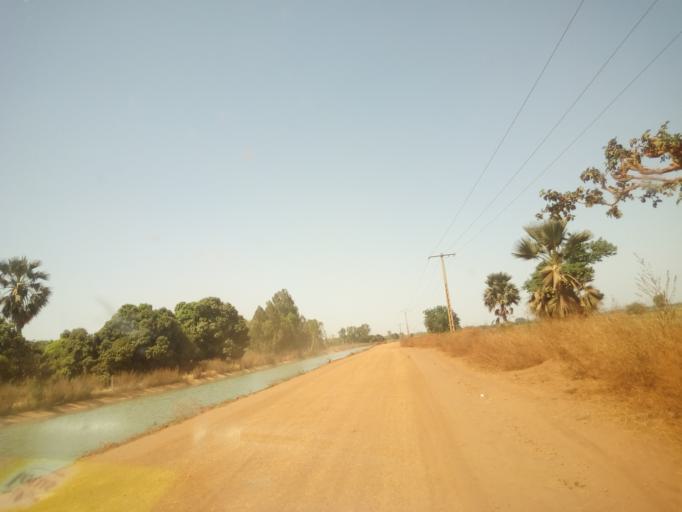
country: ML
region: Bamako
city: Bamako
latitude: 12.6218
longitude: -7.7611
